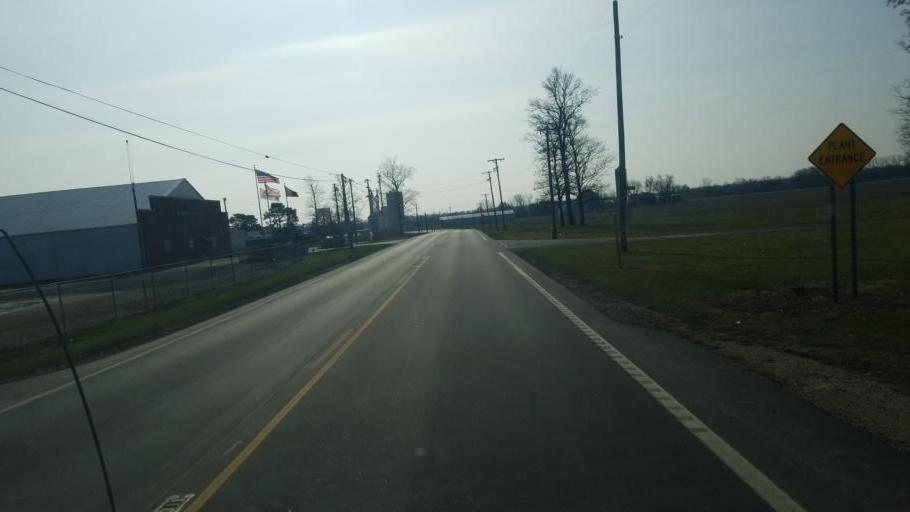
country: US
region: Ohio
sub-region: Mercer County
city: Fort Recovery
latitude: 40.4218
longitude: -84.7847
